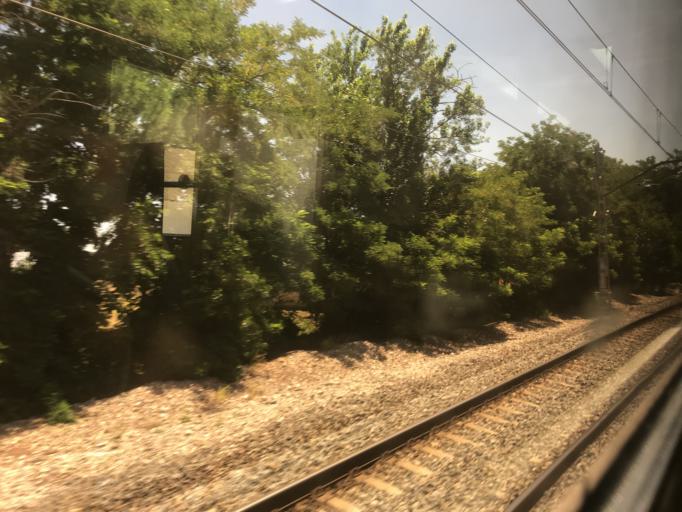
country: ES
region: Madrid
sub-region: Provincia de Madrid
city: Aranjuez
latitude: 40.0476
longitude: -3.6232
